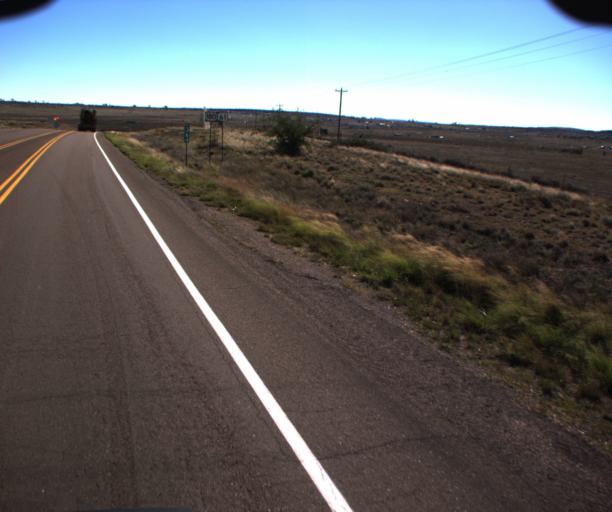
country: US
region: Arizona
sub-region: Apache County
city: Saint Johns
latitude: 34.5105
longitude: -109.4472
